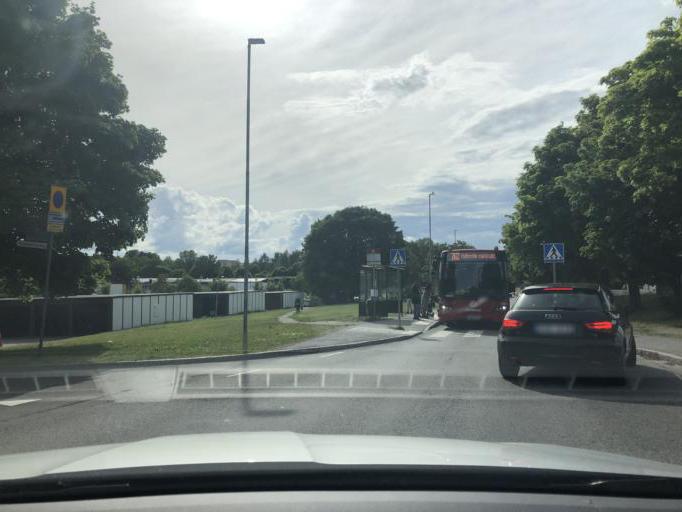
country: SE
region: Stockholm
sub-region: Botkyrka Kommun
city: Fittja
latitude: 59.2475
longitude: 17.8513
